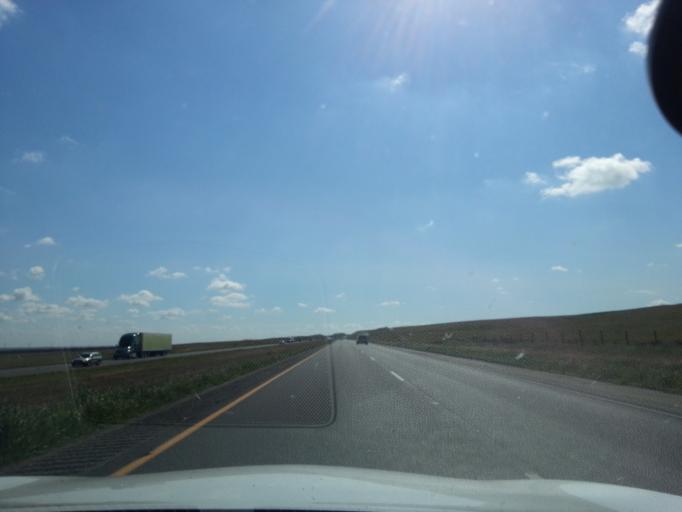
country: US
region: California
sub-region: Fresno County
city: Coalinga
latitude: 36.3406
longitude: -120.3093
